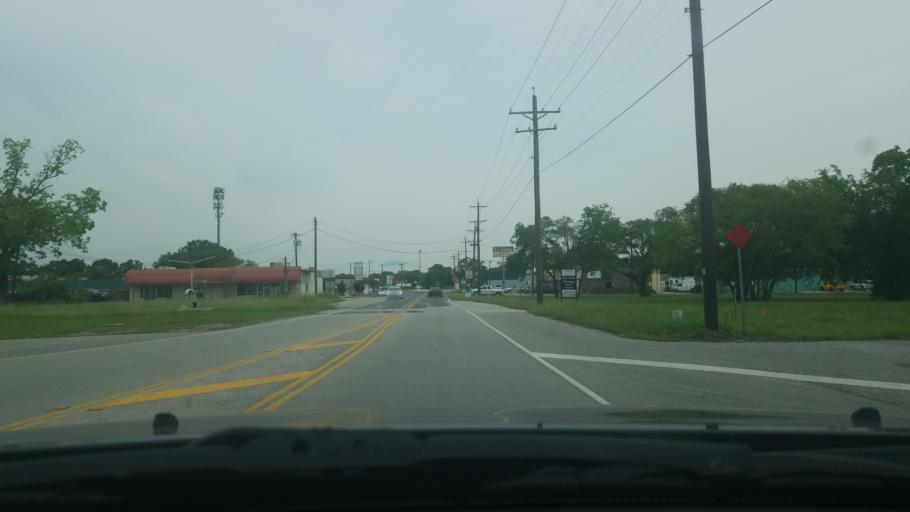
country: US
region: Texas
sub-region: Denton County
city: Lake Dallas
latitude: 33.1141
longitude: -97.0277
